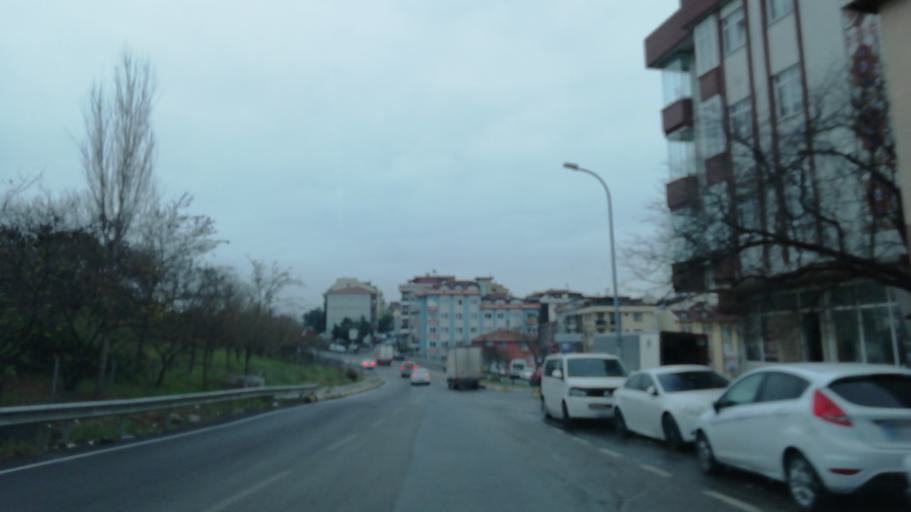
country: TR
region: Istanbul
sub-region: Atasehir
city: Atasehir
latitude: 41.0063
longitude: 29.0775
